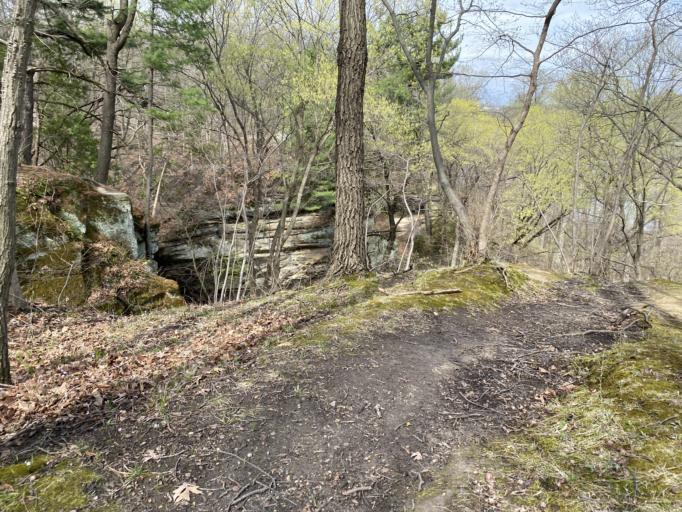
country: US
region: Illinois
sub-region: LaSalle County
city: Deer Park
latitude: 41.3142
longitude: -88.9731
